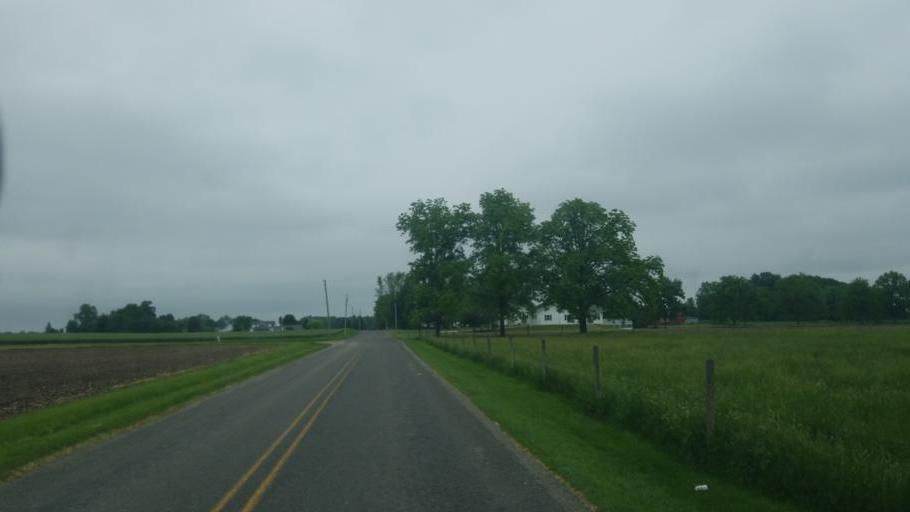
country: US
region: Indiana
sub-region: Elkhart County
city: Nappanee
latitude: 41.4637
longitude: -86.0497
